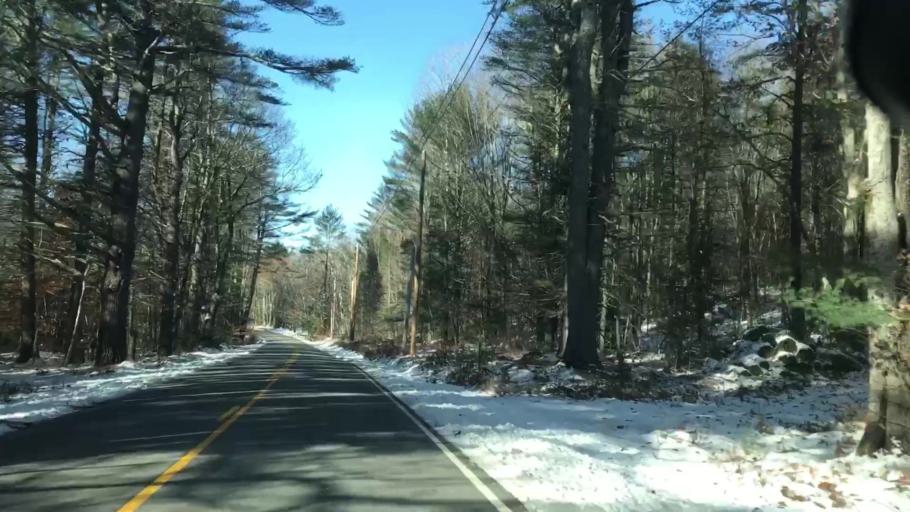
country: US
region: Maine
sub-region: Oxford County
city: Brownfield
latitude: 43.9643
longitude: -70.8657
